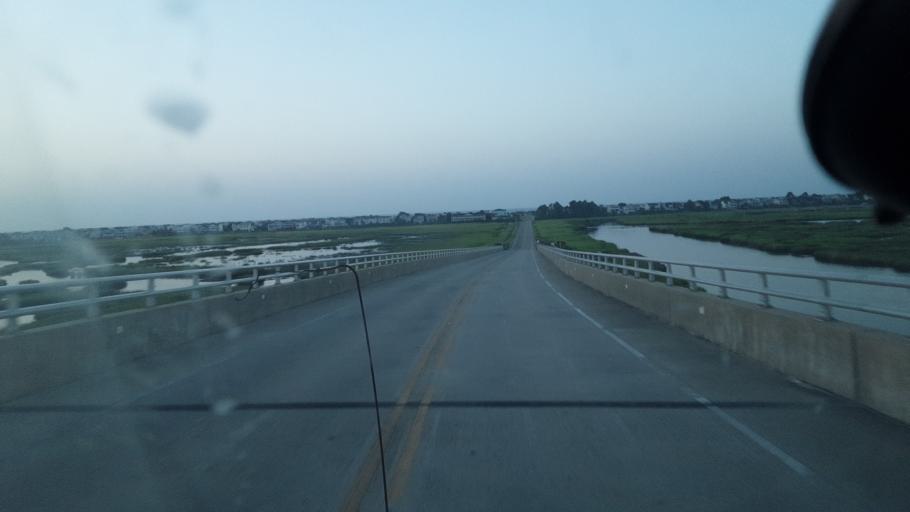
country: US
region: North Carolina
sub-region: Brunswick County
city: Sunset Beach
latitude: 33.8797
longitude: -78.5104
